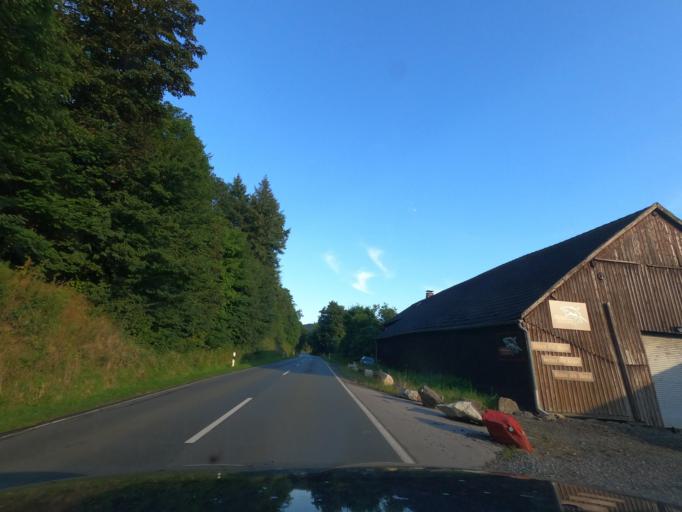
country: DE
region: North Rhine-Westphalia
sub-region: Regierungsbezirk Arnsberg
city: Sundern
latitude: 51.2947
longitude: 7.9535
